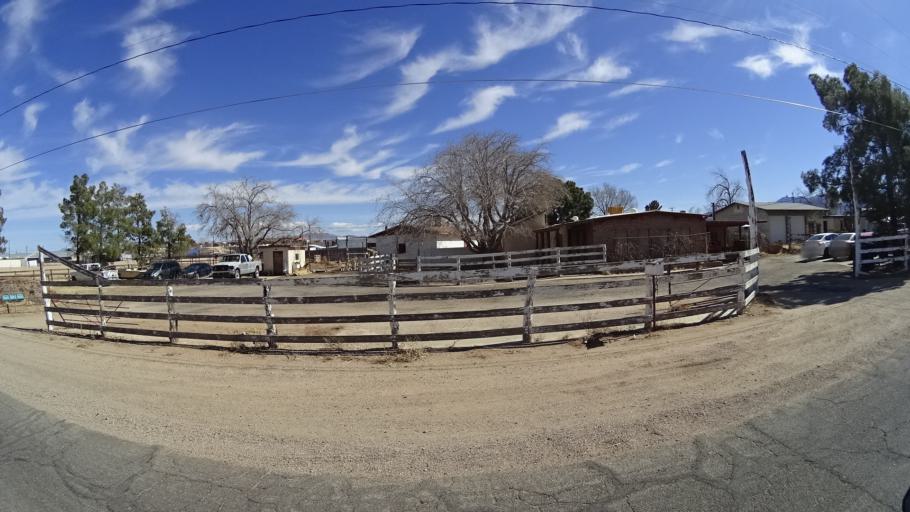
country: US
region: Arizona
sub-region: Mohave County
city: New Kingman-Butler
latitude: 35.2430
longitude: -114.0132
